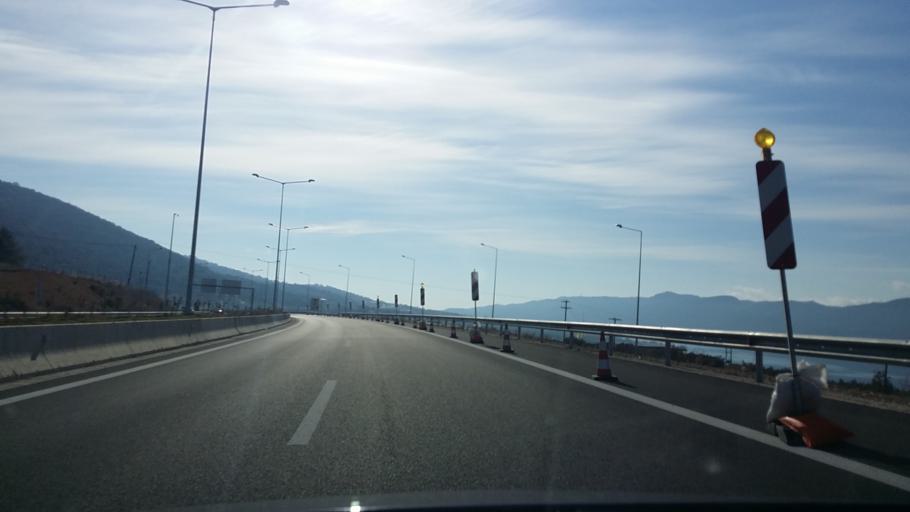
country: GR
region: West Greece
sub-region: Nomos Aitolias kai Akarnanias
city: Stanos
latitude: 38.7756
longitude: 21.1966
